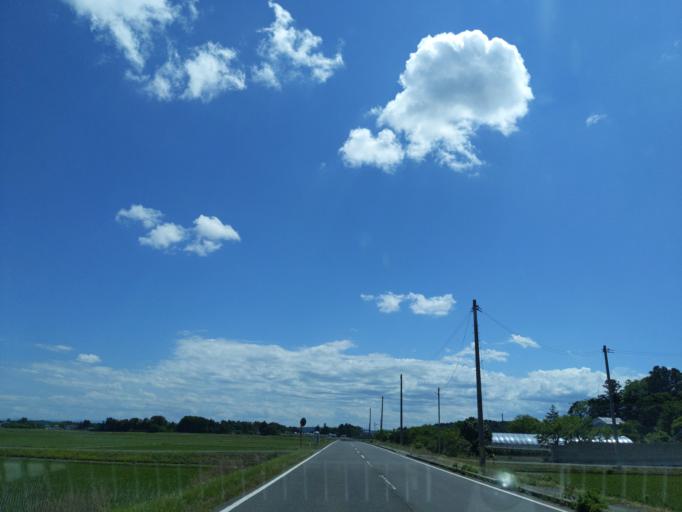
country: JP
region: Fukushima
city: Koriyama
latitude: 37.3865
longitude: 140.3005
